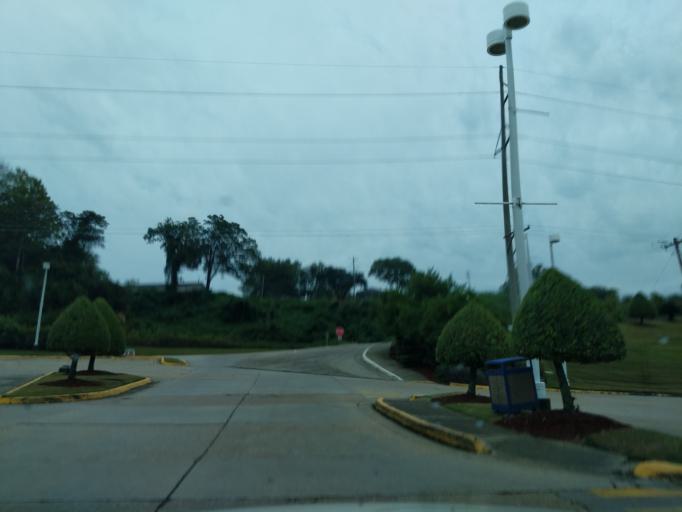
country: US
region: Mississippi
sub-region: Warren County
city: Vicksburg
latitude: 32.3247
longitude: -90.8956
